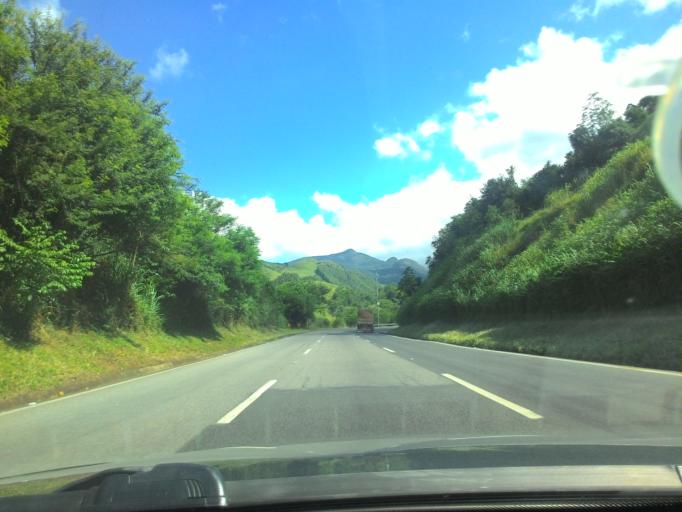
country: BR
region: Sao Paulo
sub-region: Cajati
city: Cajati
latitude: -24.8243
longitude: -48.2182
